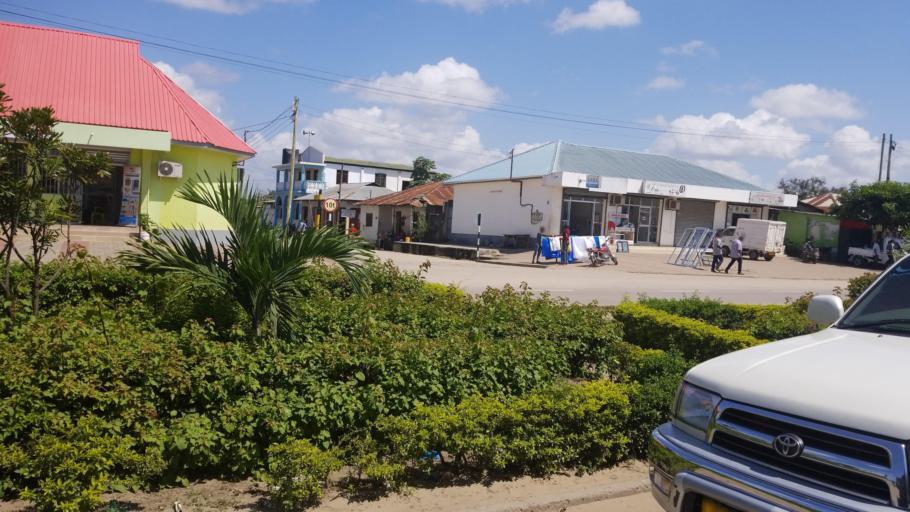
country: TZ
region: Tanga
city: Tanga
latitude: -5.0828
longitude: 39.0978
